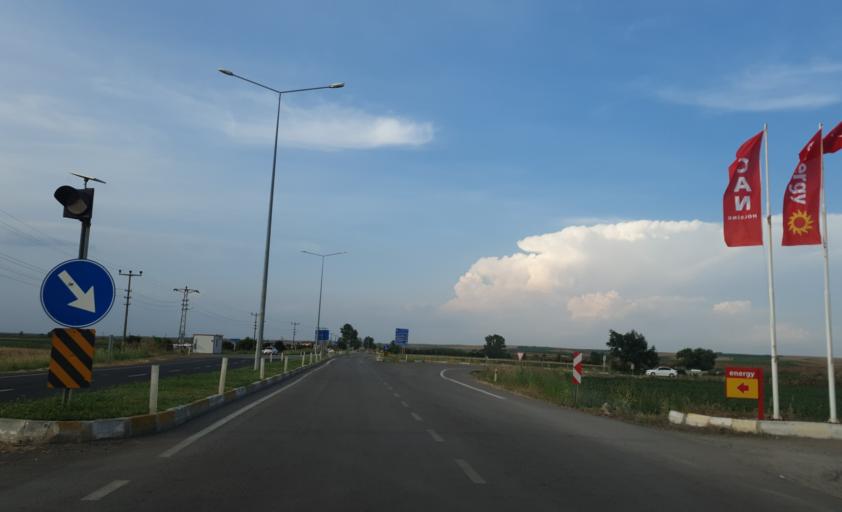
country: TR
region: Tekirdag
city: Hayrabolu
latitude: 41.2252
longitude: 27.1178
